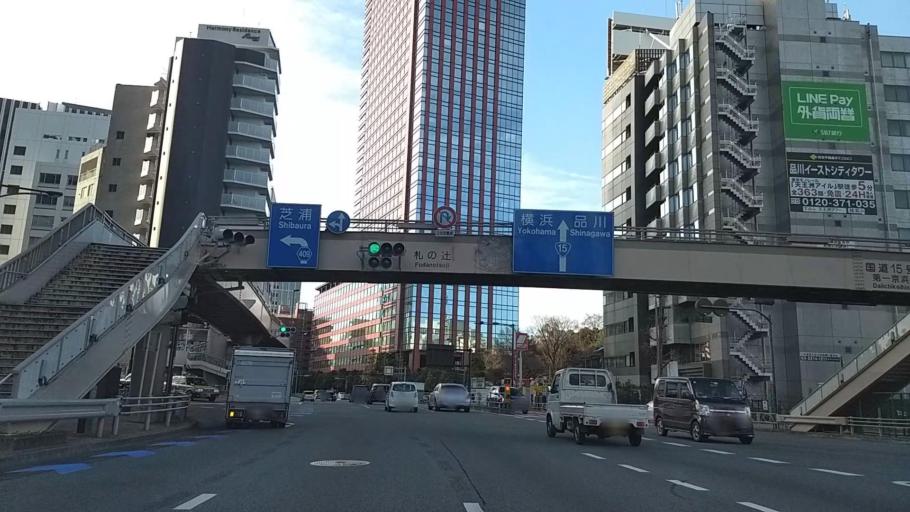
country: JP
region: Tokyo
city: Tokyo
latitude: 35.6454
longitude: 139.7445
